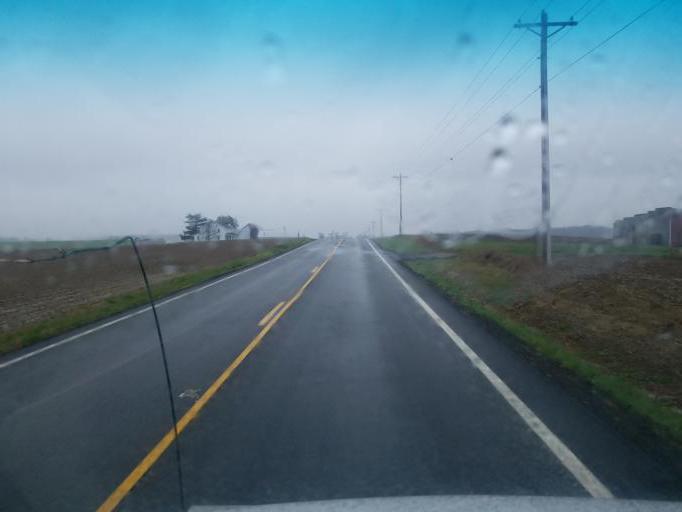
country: US
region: Ohio
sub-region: Crawford County
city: Bucyrus
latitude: 40.9648
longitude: -82.9187
